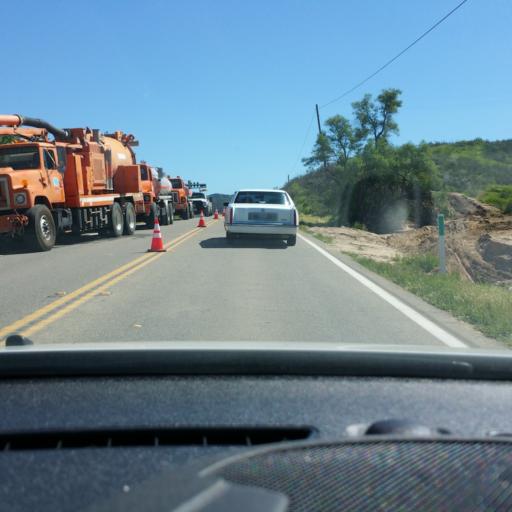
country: US
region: California
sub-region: Riverside County
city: Temecula
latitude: 33.4874
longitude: -117.0512
